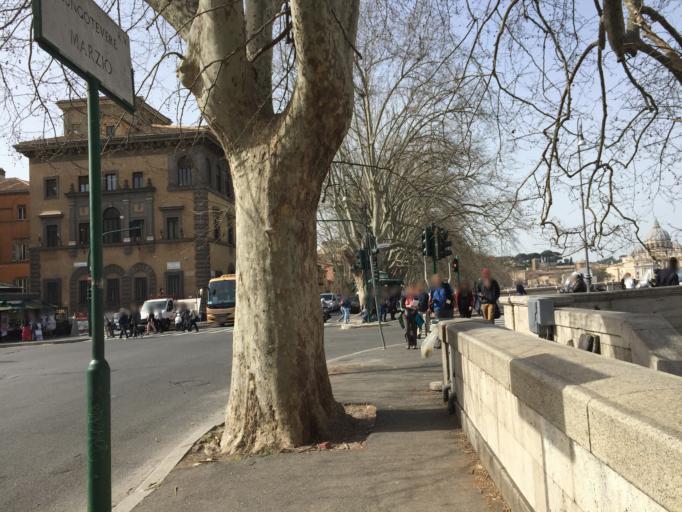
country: VA
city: Vatican City
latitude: 41.9023
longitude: 12.4719
